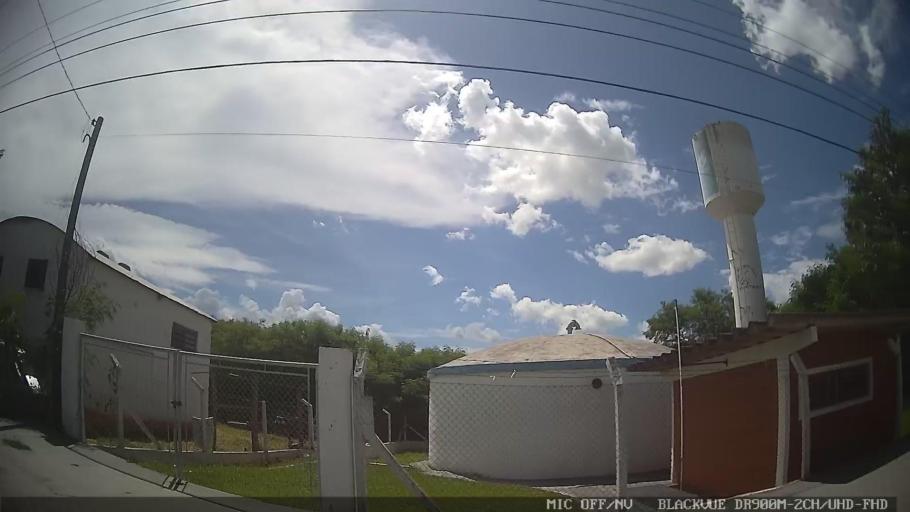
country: BR
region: Sao Paulo
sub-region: Conchas
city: Conchas
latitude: -23.0382
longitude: -48.0187
